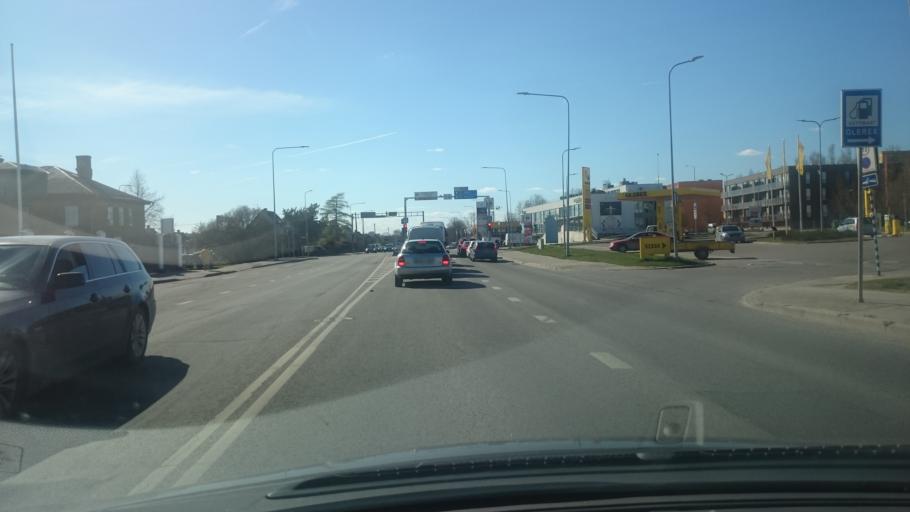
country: EE
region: Tartu
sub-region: Tartu linn
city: Tartu
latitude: 58.3807
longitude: 26.7555
